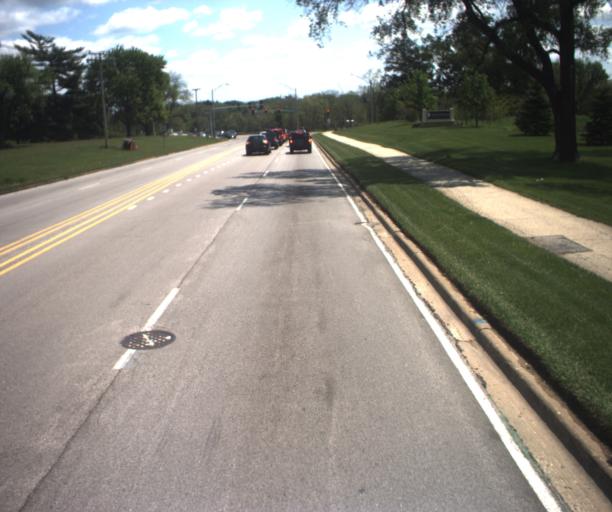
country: US
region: Illinois
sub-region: Kane County
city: Batavia
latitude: 41.8644
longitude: -88.3139
